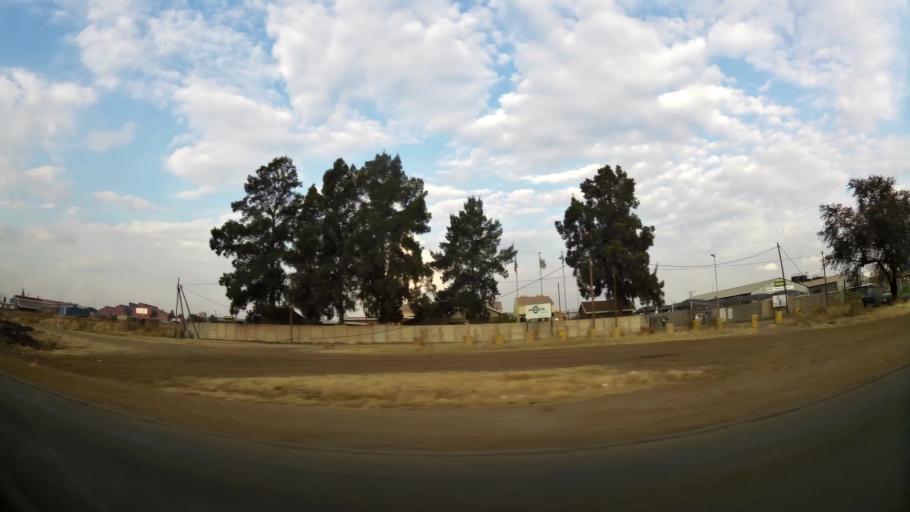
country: ZA
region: Gauteng
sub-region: Sedibeng District Municipality
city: Vanderbijlpark
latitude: -26.6721
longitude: 27.7923
